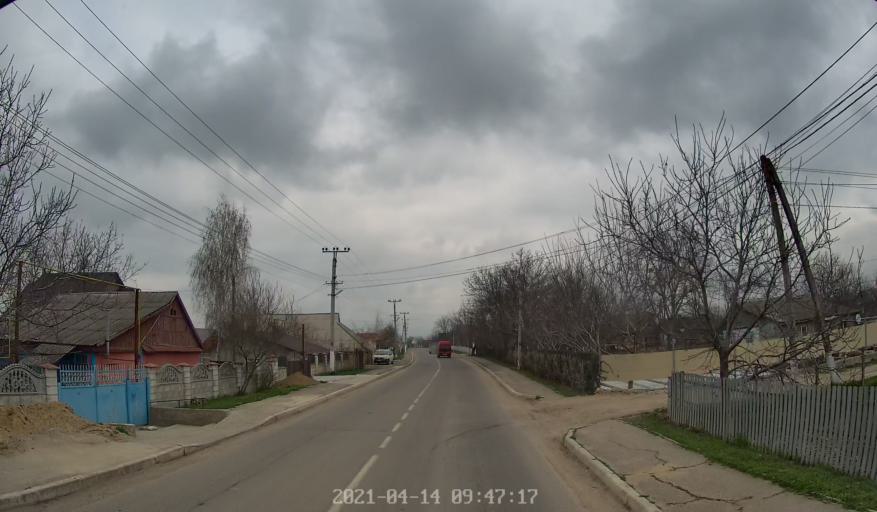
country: MD
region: Chisinau
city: Vadul lui Voda
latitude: 47.1370
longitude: 29.1197
